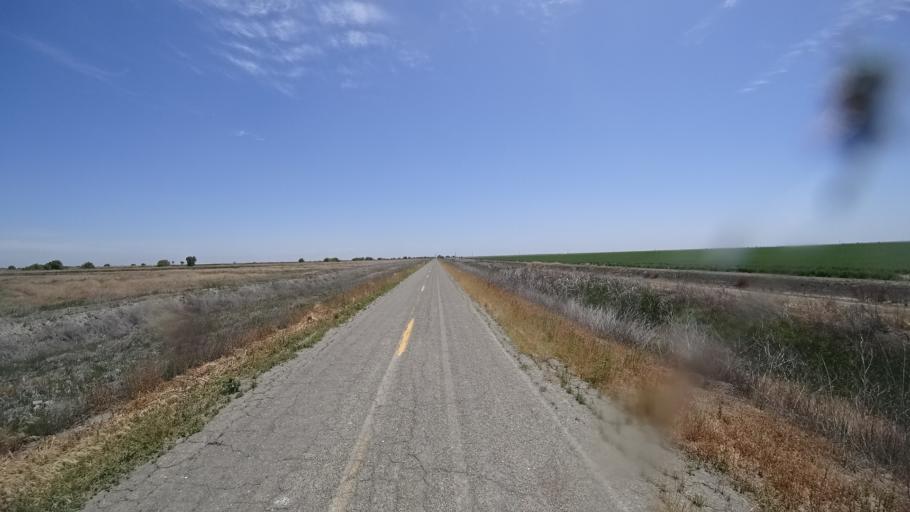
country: US
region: California
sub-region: Kings County
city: Stratford
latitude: 36.1379
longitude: -119.7421
